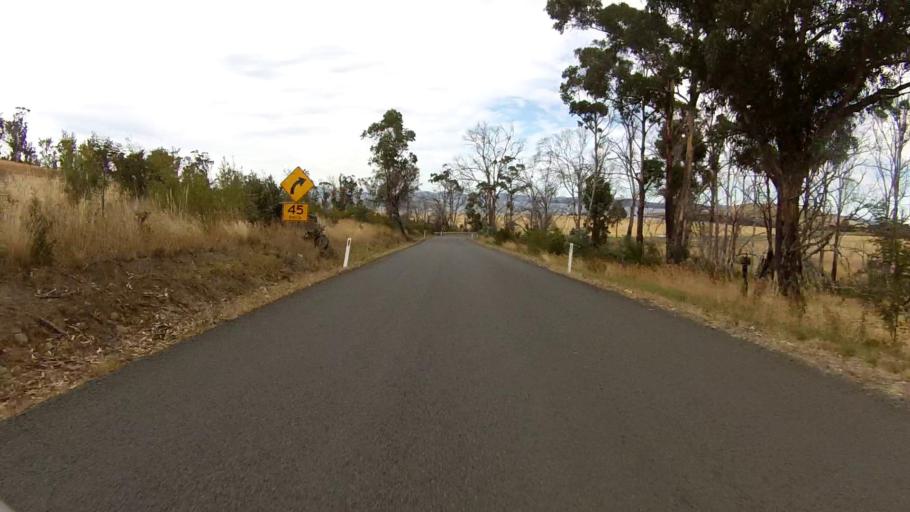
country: AU
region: Tasmania
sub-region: Sorell
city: Sorell
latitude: -42.8932
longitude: 147.7796
